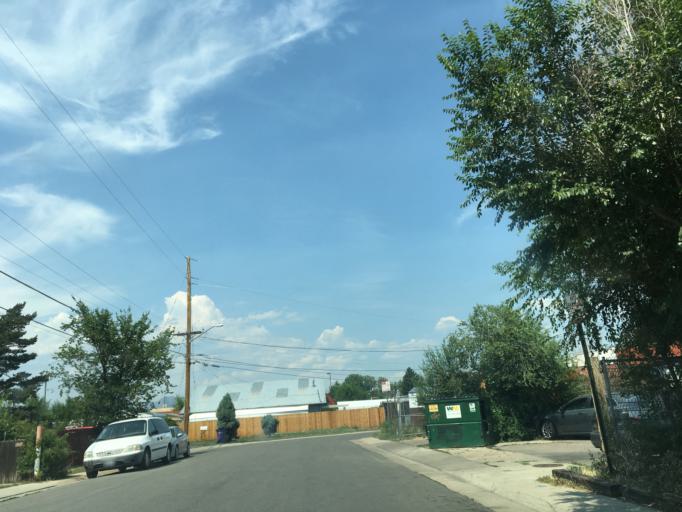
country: US
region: Colorado
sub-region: Jefferson County
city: Lakewood
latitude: 39.6976
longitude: -105.0503
